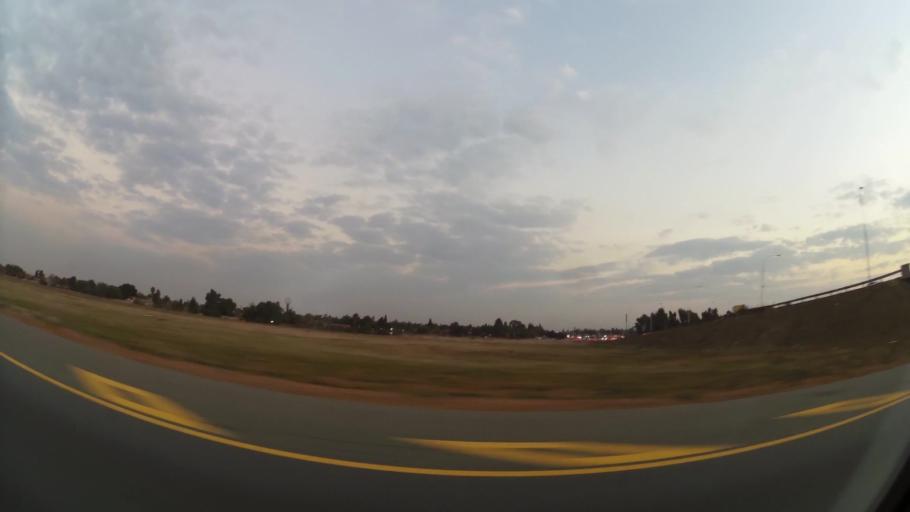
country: ZA
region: Gauteng
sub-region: Ekurhuleni Metropolitan Municipality
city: Boksburg
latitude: -26.2517
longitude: 28.2455
